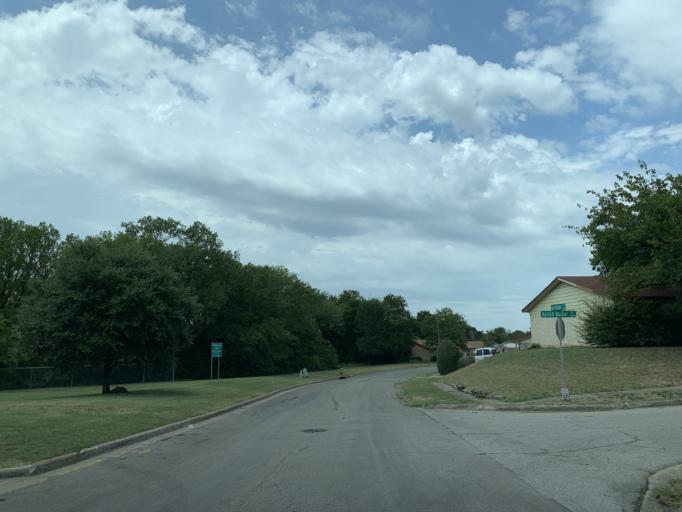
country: US
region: Texas
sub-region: Dallas County
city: DeSoto
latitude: 32.6582
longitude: -96.8133
